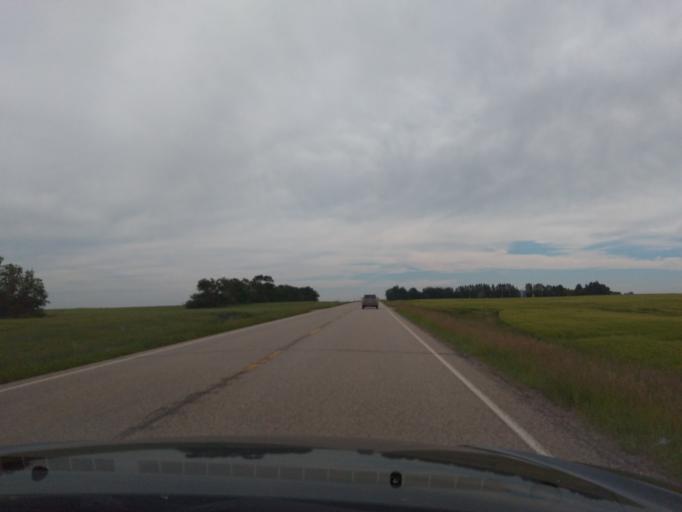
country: CA
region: Alberta
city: Irricana
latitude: 51.5034
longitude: -113.7265
